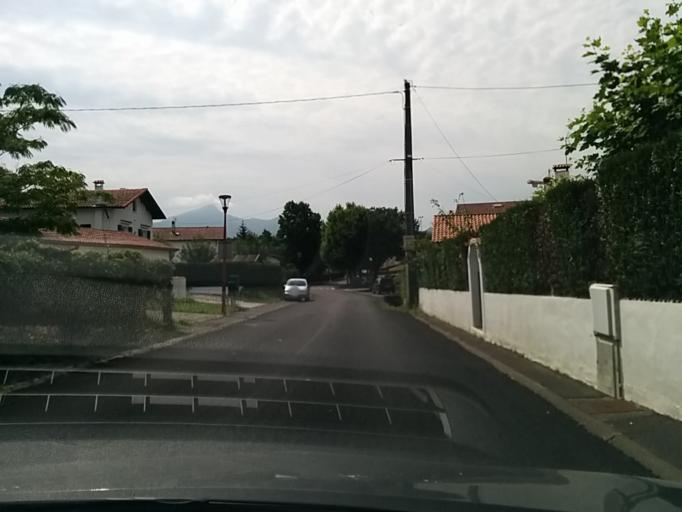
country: FR
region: Aquitaine
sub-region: Departement des Pyrenees-Atlantiques
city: Urrugne
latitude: 43.3653
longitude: -1.6991
